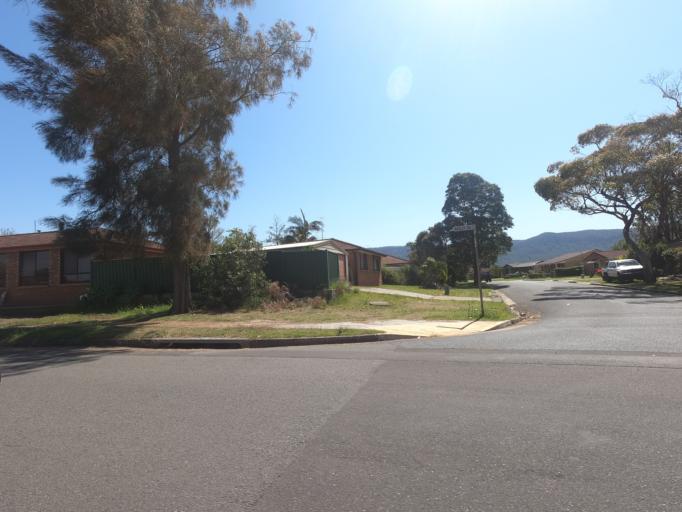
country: AU
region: New South Wales
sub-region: Wollongong
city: Dapto
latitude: -34.4837
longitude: 150.7822
